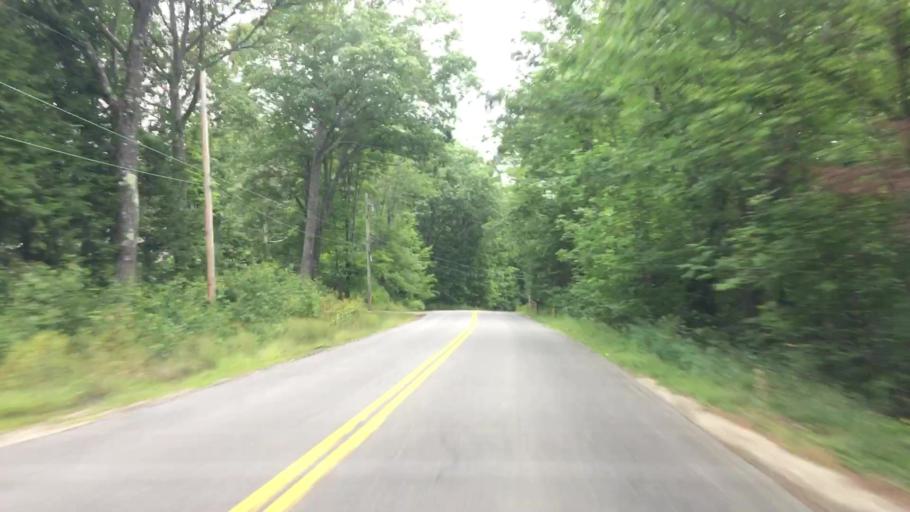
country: US
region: Maine
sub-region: Cumberland County
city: New Gloucester
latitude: 43.9057
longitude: -70.2157
